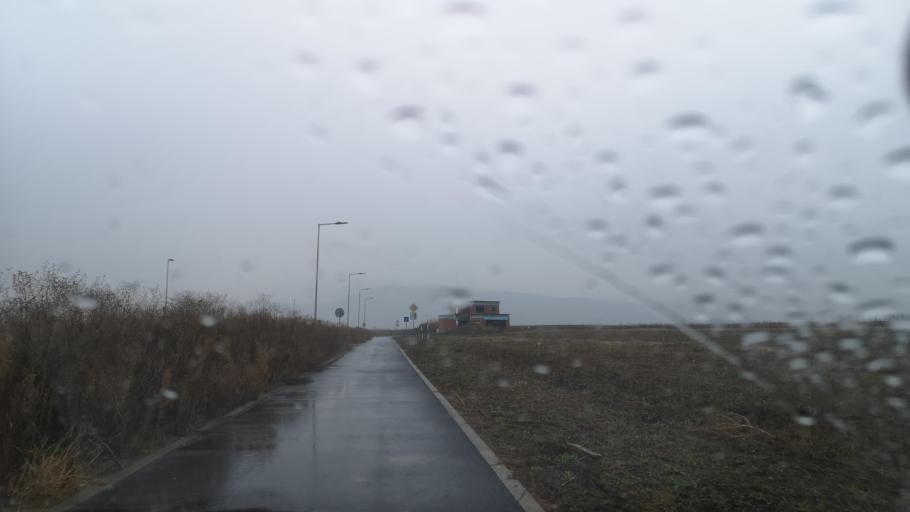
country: SK
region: Nitriansky
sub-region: Okres Nitra
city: Nitra
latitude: 48.2958
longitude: 18.1329
